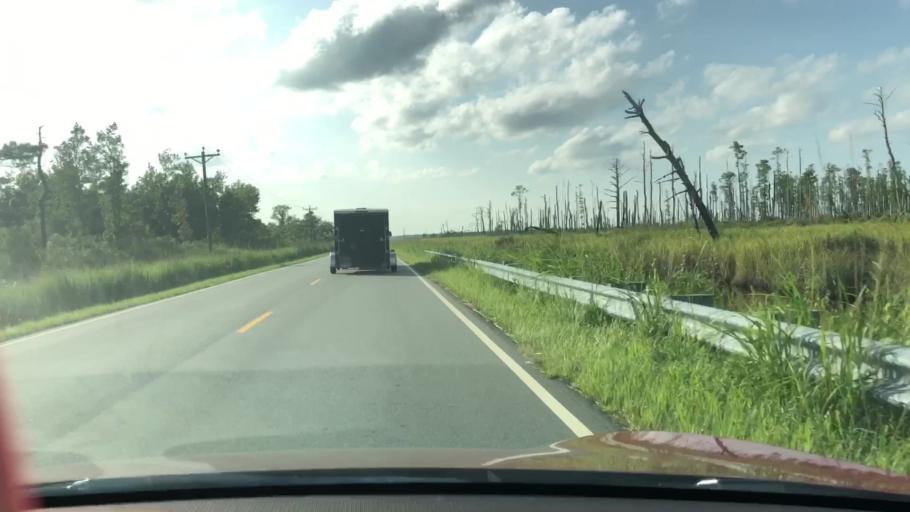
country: US
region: North Carolina
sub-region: Dare County
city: Wanchese
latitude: 35.6205
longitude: -75.8382
